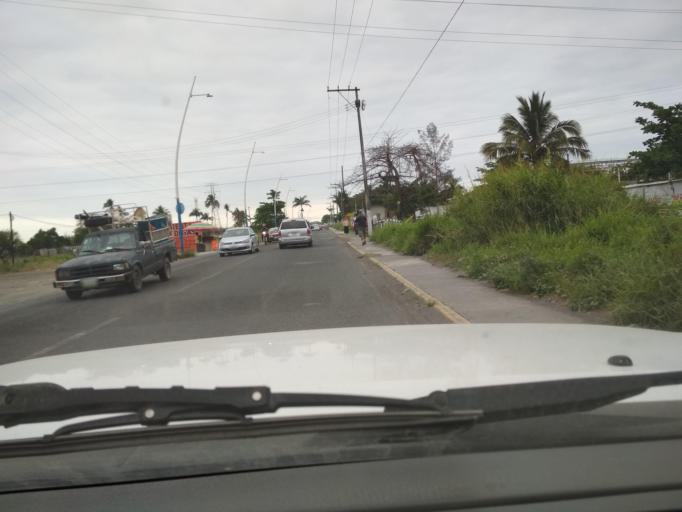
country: MX
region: Veracruz
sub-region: Medellin
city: Fraccionamiento Arboledas San Ramon
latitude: 19.0845
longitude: -96.1563
